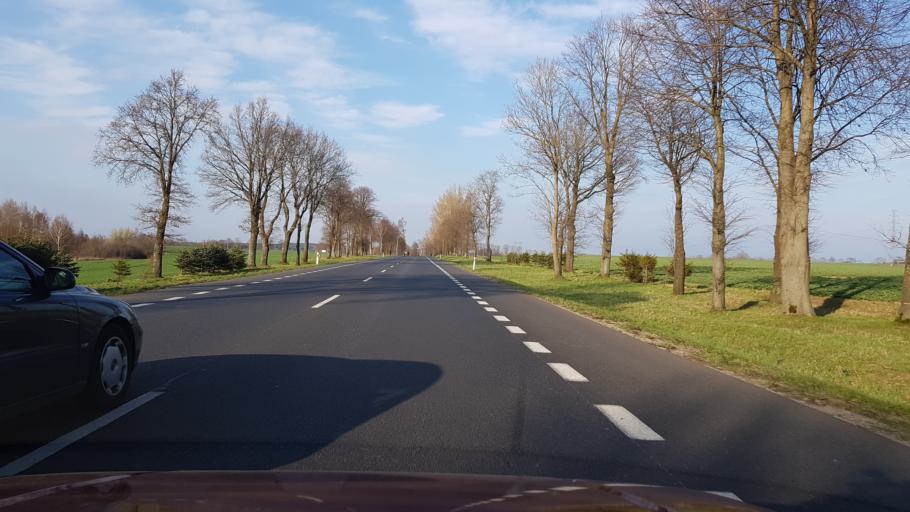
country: PL
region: West Pomeranian Voivodeship
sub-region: Koszalin
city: Koszalin
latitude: 54.1467
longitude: 16.0698
